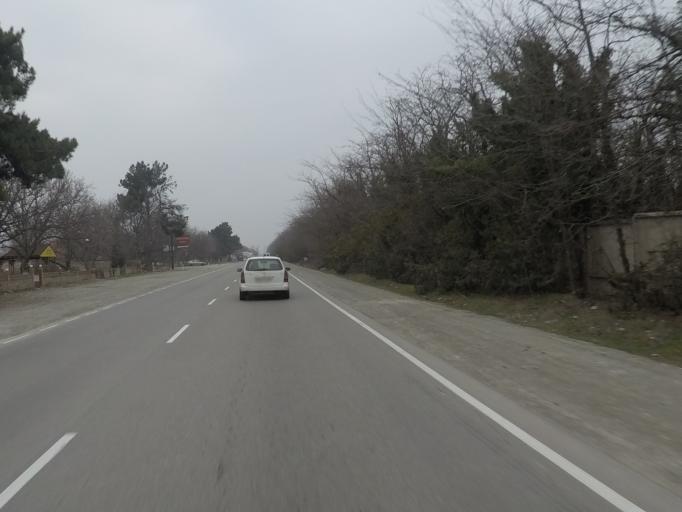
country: GE
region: Mtskheta-Mtianeti
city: Mtskheta
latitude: 41.8987
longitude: 44.7203
